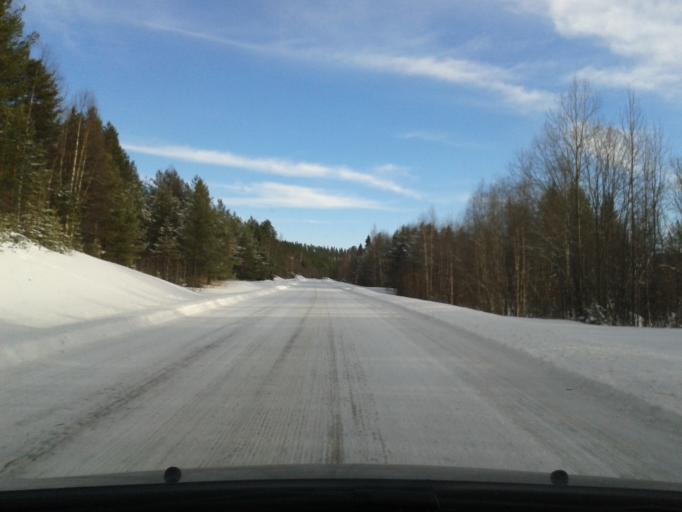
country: SE
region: Vaesterbotten
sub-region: Asele Kommun
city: Asele
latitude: 64.3216
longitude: 17.1038
